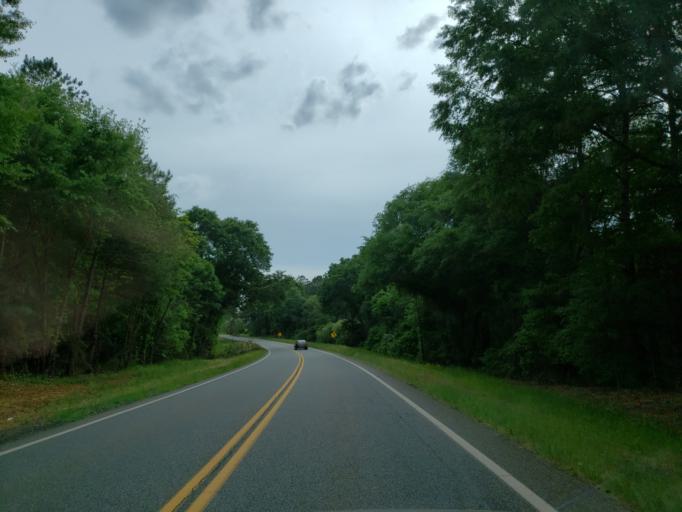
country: US
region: Georgia
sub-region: Macon County
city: Marshallville
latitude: 32.4138
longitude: -83.8635
